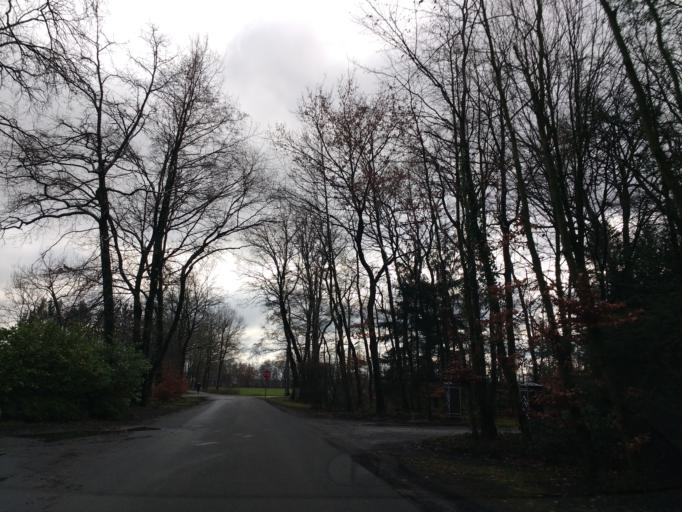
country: DE
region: North Rhine-Westphalia
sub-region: Regierungsbezirk Detmold
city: Hovelhof
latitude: 51.8216
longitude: 8.6918
